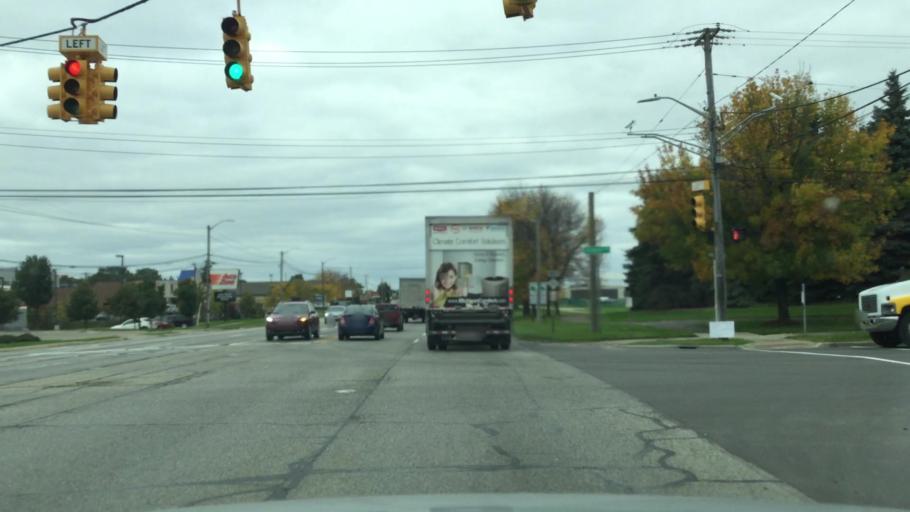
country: US
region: Michigan
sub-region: Oakland County
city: Waterford
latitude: 42.6600
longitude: -83.4058
